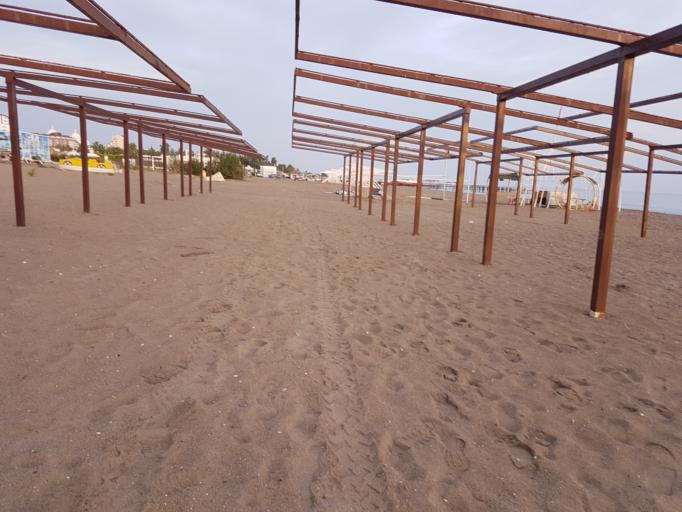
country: TR
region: Antalya
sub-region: Serik
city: Kumkoey
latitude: 36.8534
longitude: 30.8859
